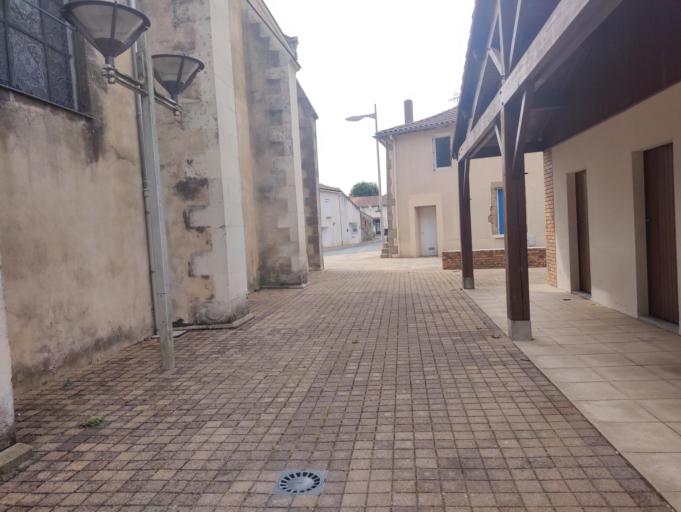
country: FR
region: Pays de la Loire
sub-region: Departement de Maine-et-Loire
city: Yzernay
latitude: 47.0213
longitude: -0.7043
